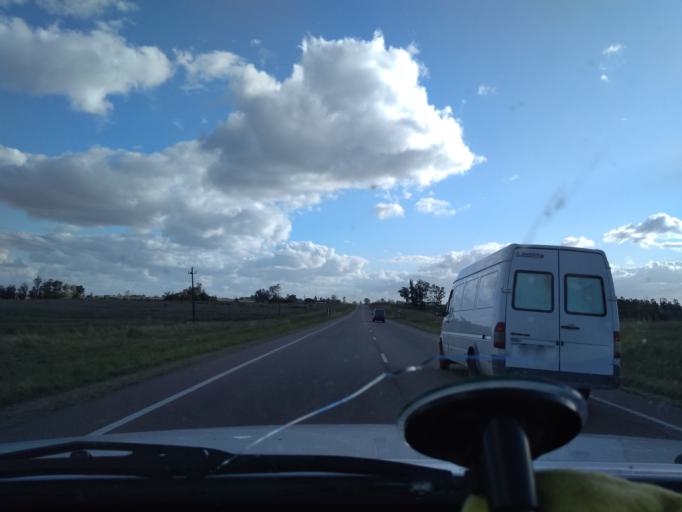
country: UY
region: Canelones
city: Tala
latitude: -34.4234
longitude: -55.8139
